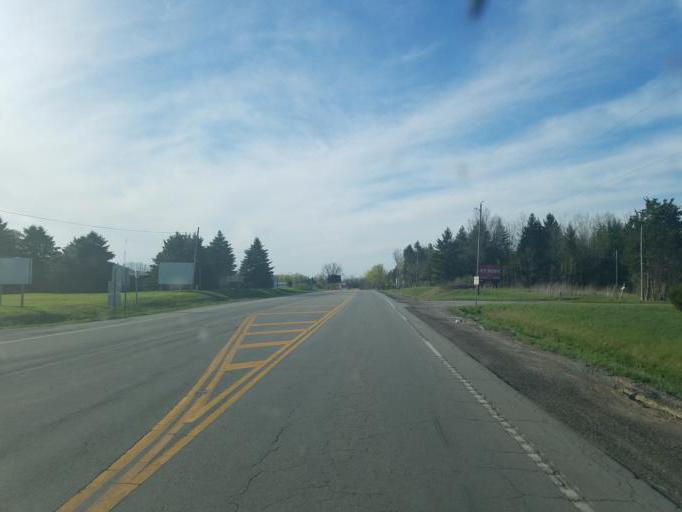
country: US
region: Ohio
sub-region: Huron County
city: New London
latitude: 41.0299
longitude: -82.4180
